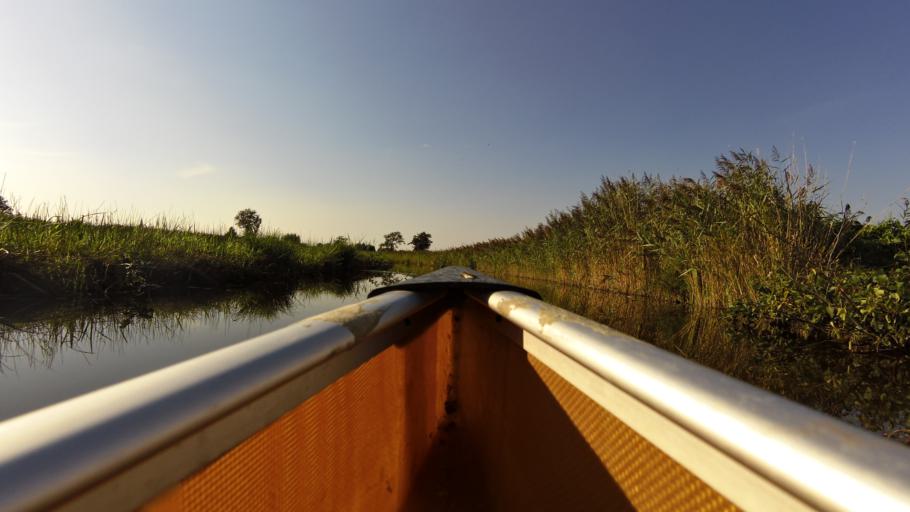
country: NL
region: South Holland
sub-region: Gemeente Nieuwkoop
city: Nieuwkoop
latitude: 52.1476
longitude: 4.7888
